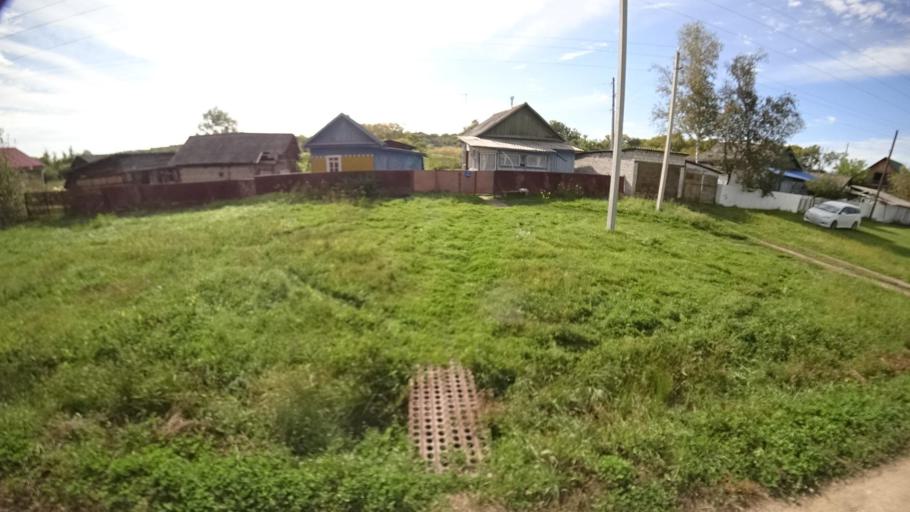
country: RU
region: Primorskiy
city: Dostoyevka
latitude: 44.2994
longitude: 133.4640
